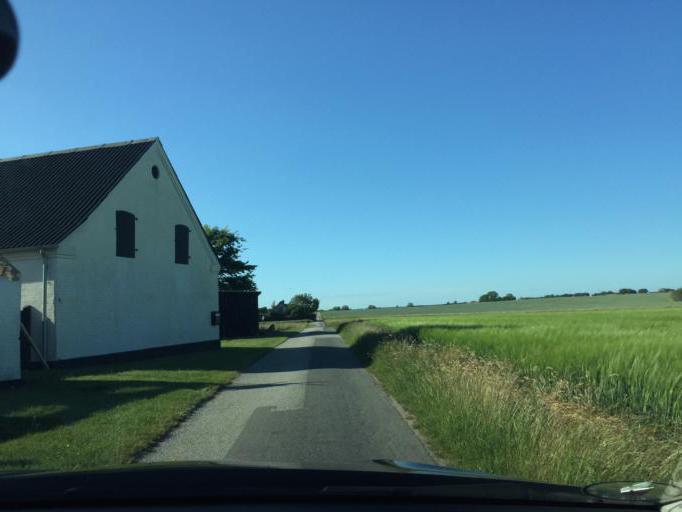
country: DK
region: Zealand
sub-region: Slagelse Kommune
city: Skaelskor
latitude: 55.1983
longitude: 11.1824
